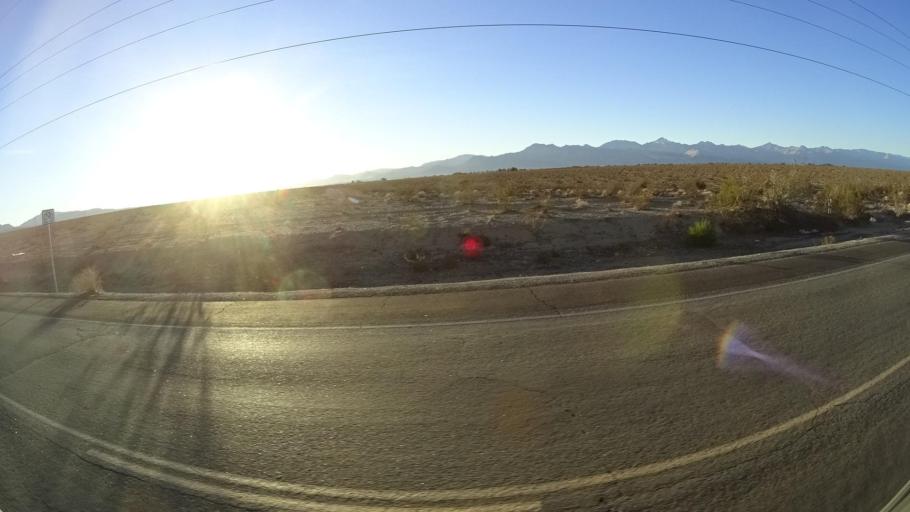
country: US
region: California
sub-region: Kern County
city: China Lake Acres
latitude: 35.6267
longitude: -117.7230
